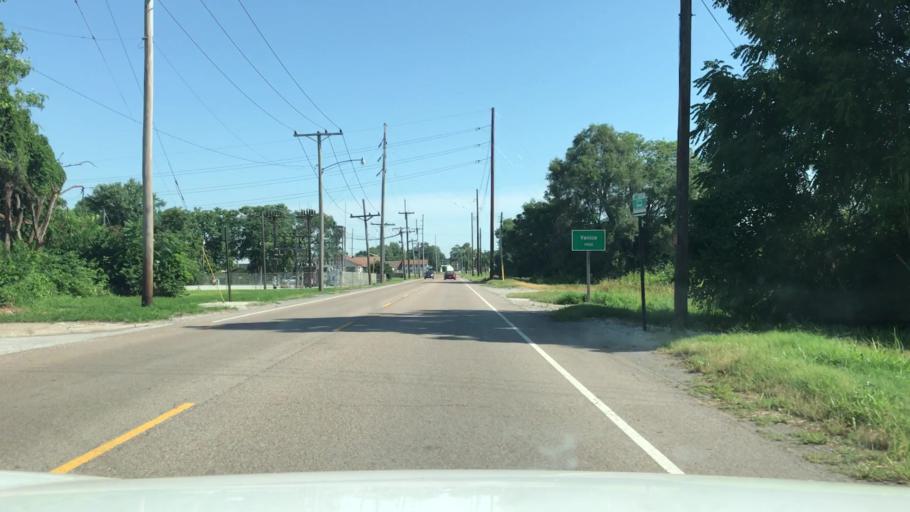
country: US
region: Illinois
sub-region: Madison County
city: Venice
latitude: 38.6658
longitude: -90.1703
